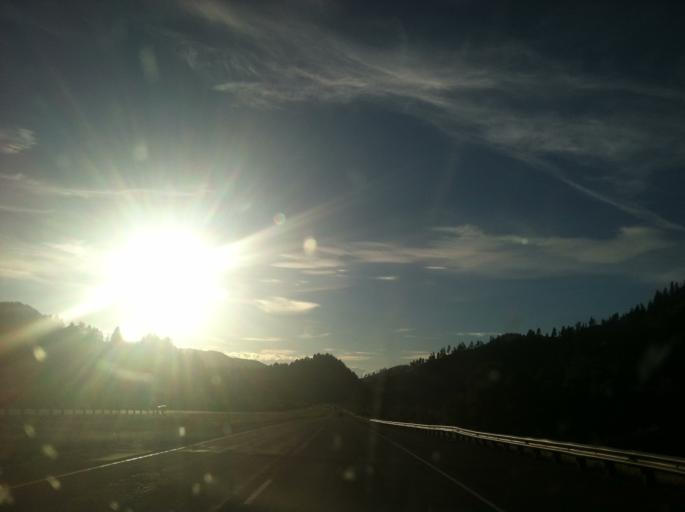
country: US
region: Montana
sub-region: Missoula County
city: Clinton
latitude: 46.6993
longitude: -113.4342
